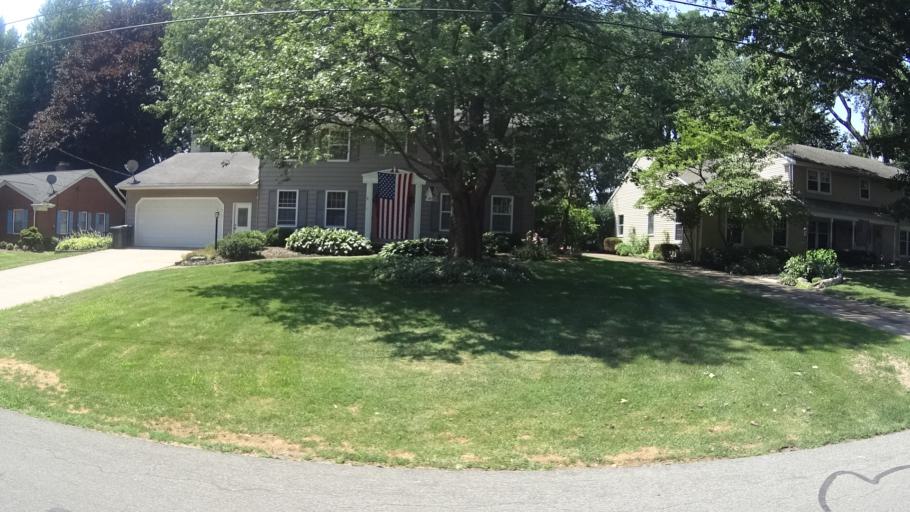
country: US
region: Ohio
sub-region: Erie County
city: Sandusky
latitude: 41.4093
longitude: -82.6449
